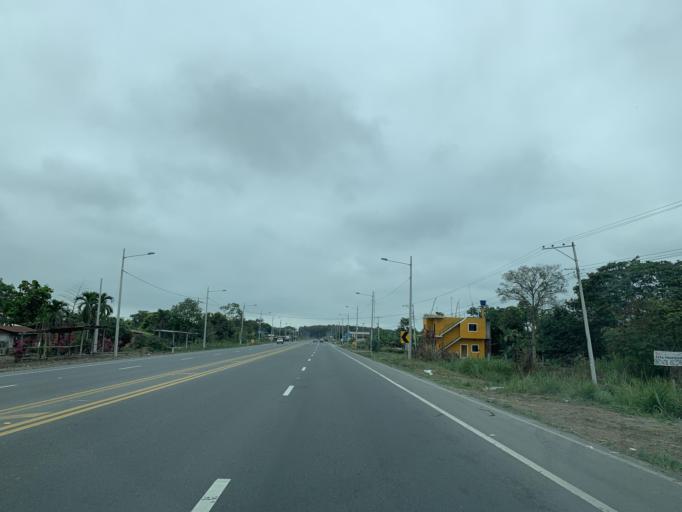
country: EC
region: Guayas
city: Coronel Marcelino Mariduena
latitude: -2.3196
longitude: -79.4650
